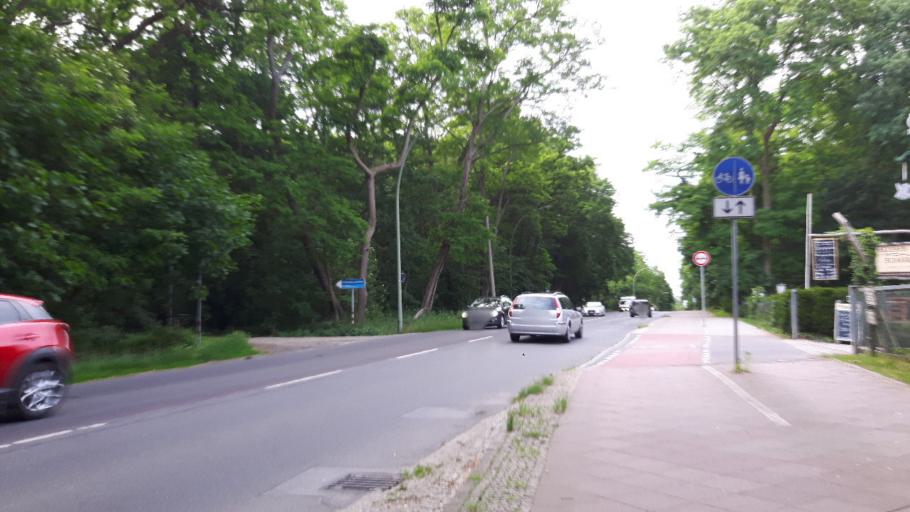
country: DE
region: Brandenburg
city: Potsdam
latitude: 52.3771
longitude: 13.0543
